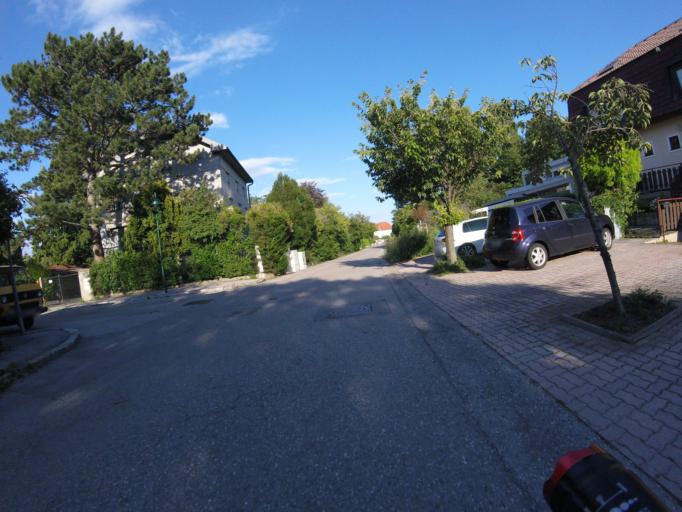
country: AT
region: Lower Austria
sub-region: Politischer Bezirk Modling
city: Wiener Neudorf
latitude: 48.0739
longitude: 16.3011
